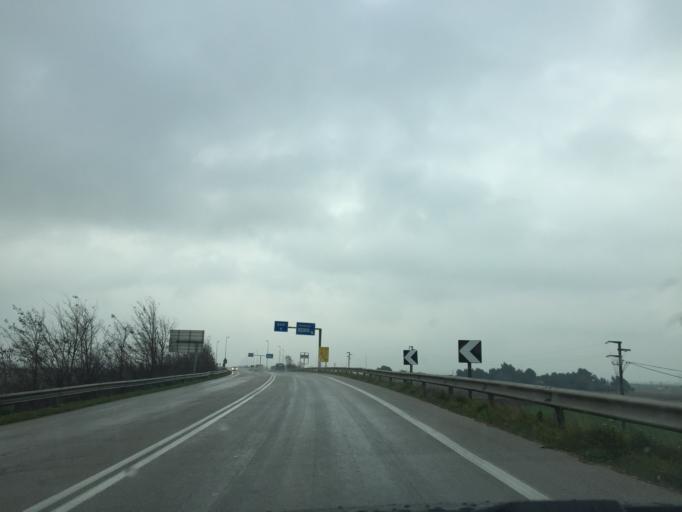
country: IT
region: Apulia
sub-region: Provincia di Foggia
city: Foggia
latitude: 41.4761
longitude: 15.5102
